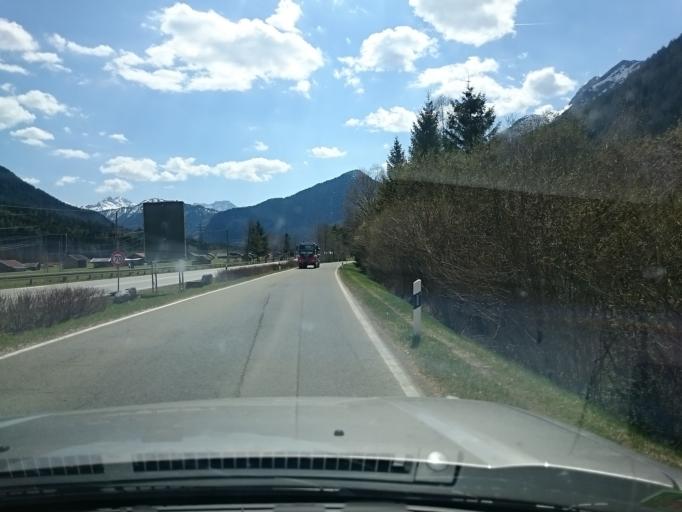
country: DE
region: Bavaria
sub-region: Upper Bavaria
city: Mittenwald
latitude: 47.4262
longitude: 11.2601
